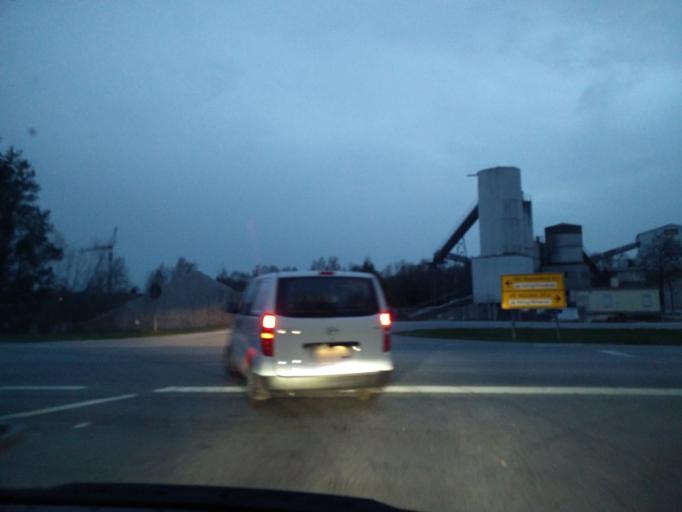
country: DE
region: Bavaria
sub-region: Upper Bavaria
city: Edling
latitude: 48.0640
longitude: 12.1668
